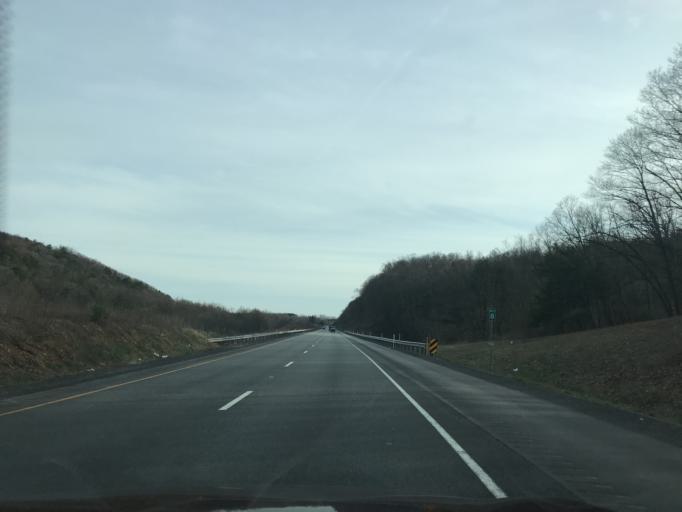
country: US
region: Pennsylvania
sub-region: Lycoming County
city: Muncy
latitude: 41.1591
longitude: -76.7974
